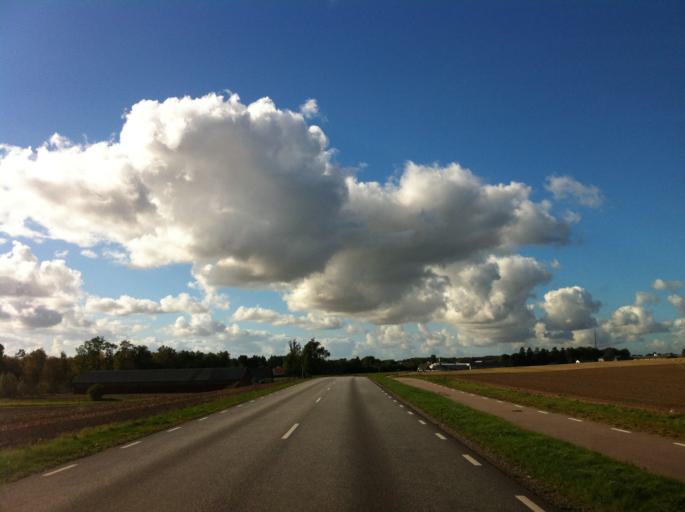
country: SE
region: Skane
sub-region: Hoors Kommun
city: Loberod
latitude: 55.7487
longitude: 13.3870
